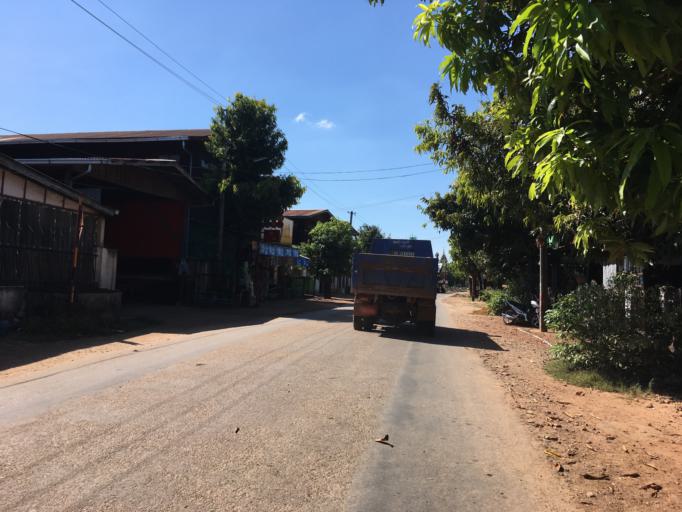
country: MM
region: Mon
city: Kyaikkami
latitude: 15.5034
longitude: 97.8362
